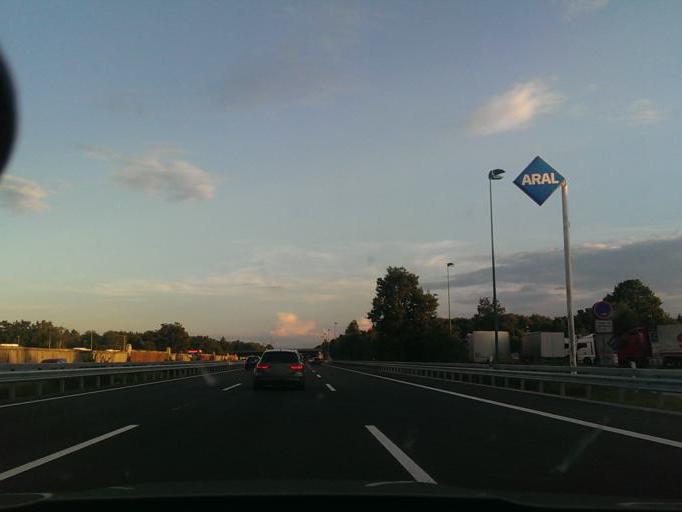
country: DE
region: Lower Saxony
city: Essel
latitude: 52.6968
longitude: 9.6866
